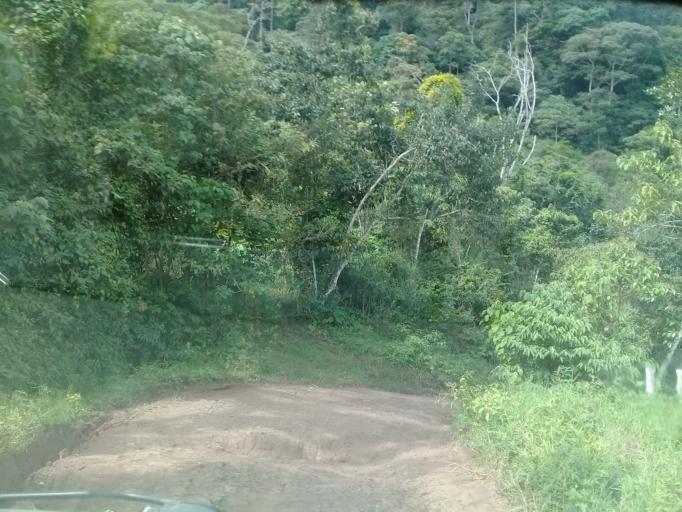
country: CO
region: Cundinamarca
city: Granada
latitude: 5.1185
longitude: -74.5679
